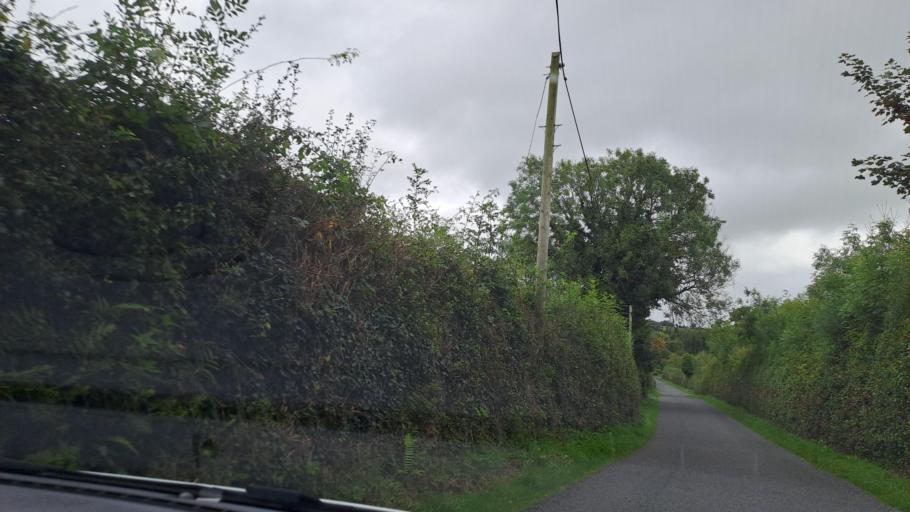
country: IE
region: Ulster
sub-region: County Monaghan
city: Carrickmacross
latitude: 54.0248
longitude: -6.7354
